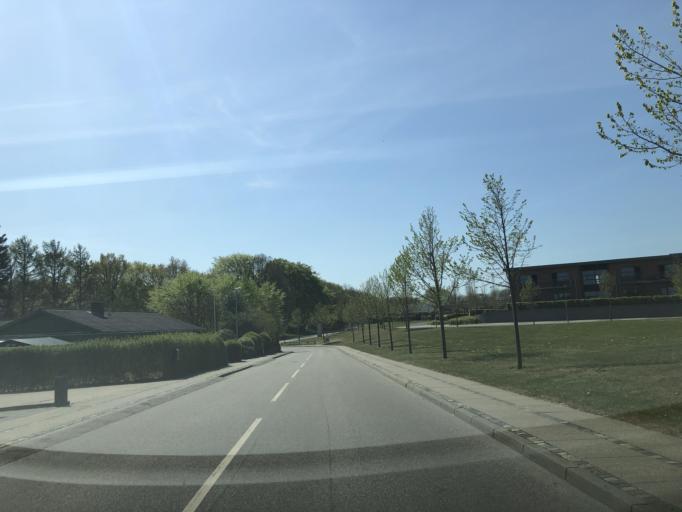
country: DK
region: North Denmark
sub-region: Mariagerfjord Kommune
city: Mariager
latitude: 56.6468
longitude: 9.9709
